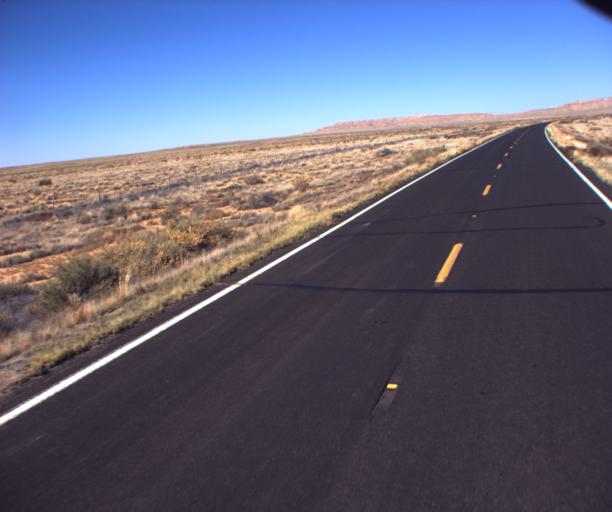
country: US
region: Arizona
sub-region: Navajo County
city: First Mesa
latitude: 35.7282
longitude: -110.5177
